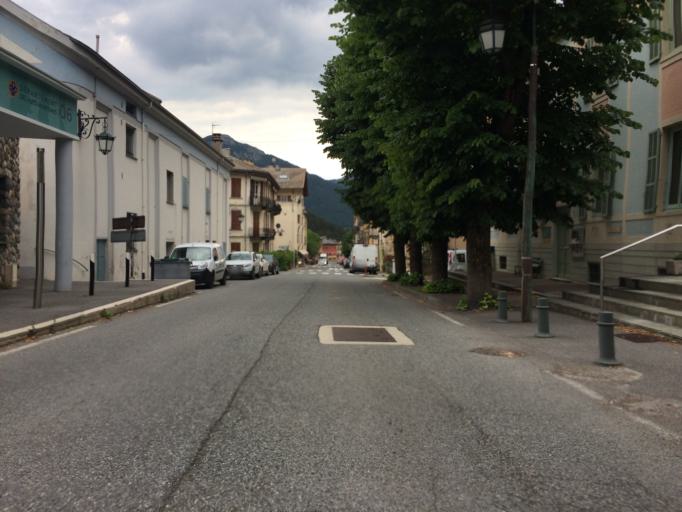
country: FR
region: Provence-Alpes-Cote d'Azur
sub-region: Departement des Alpes-Maritimes
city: Tende
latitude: 44.0903
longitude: 7.5927
